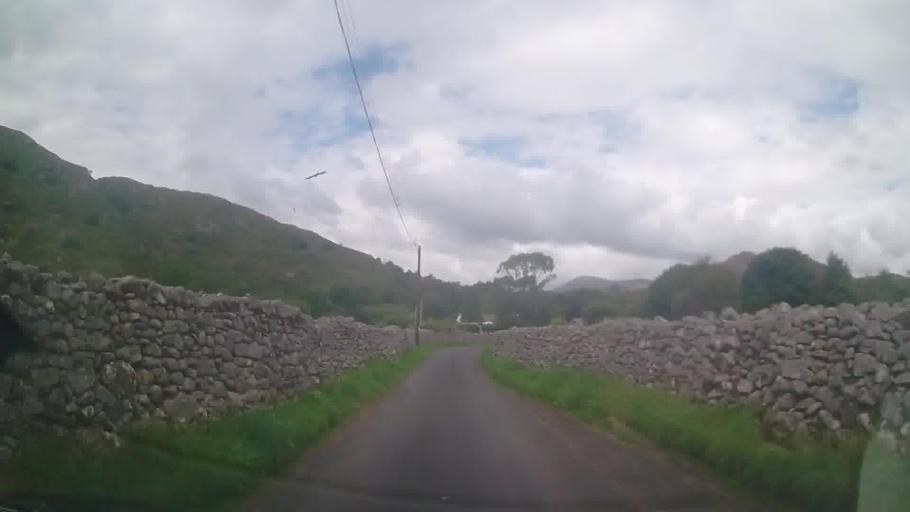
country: GB
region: England
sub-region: Cumbria
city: Millom
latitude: 54.3969
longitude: -3.2711
